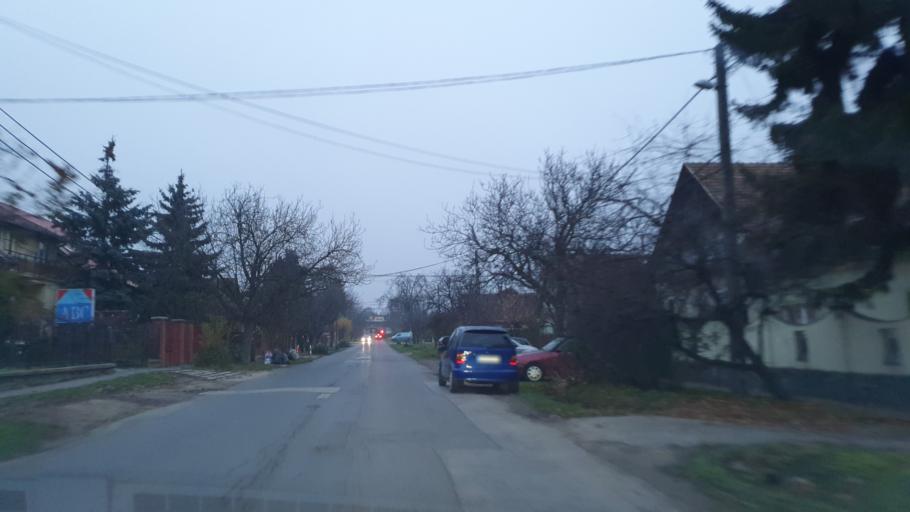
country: HU
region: Pest
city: Csomor
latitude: 47.5279
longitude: 19.2265
